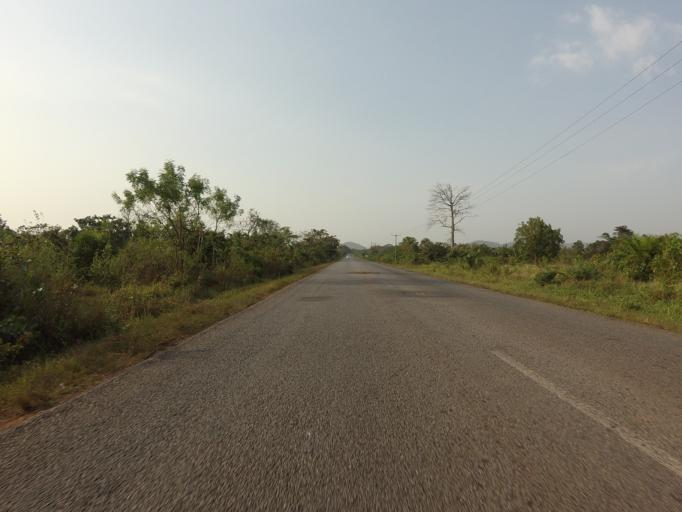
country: GH
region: Volta
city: Ho
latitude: 6.3908
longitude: 0.1829
